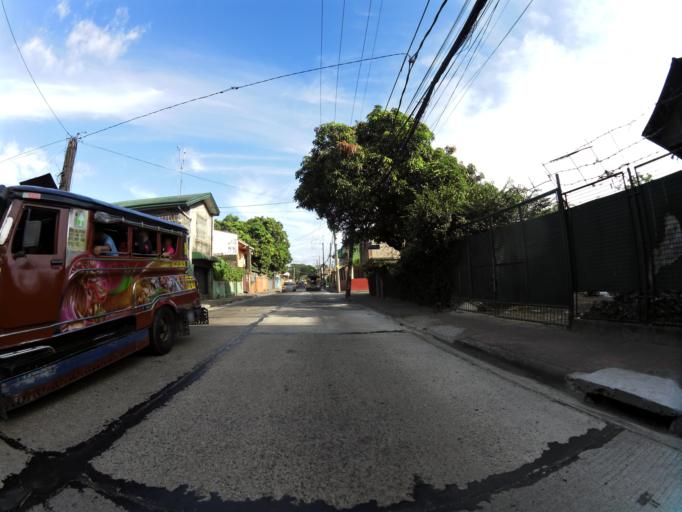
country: PH
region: Metro Manila
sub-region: Marikina
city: Calumpang
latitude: 14.6418
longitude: 121.1012
